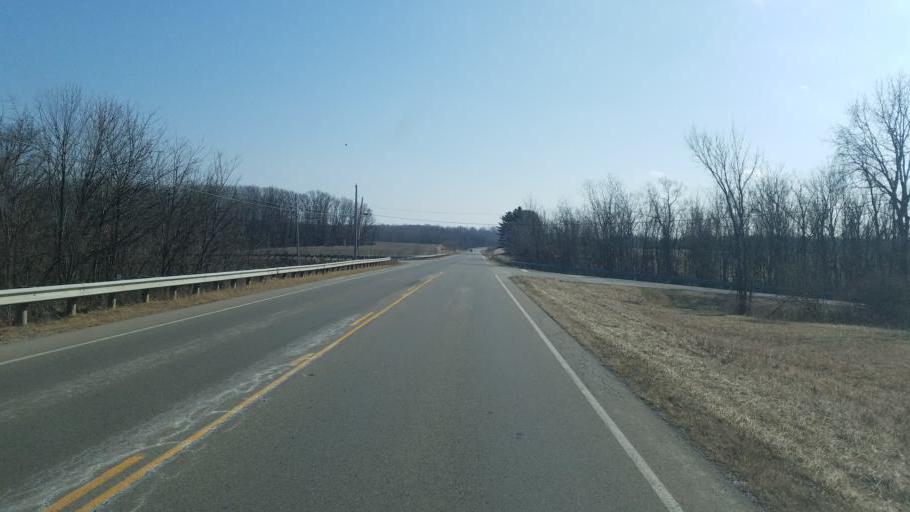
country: US
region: Ohio
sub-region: Richland County
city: Lincoln Heights
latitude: 40.8296
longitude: -82.5089
